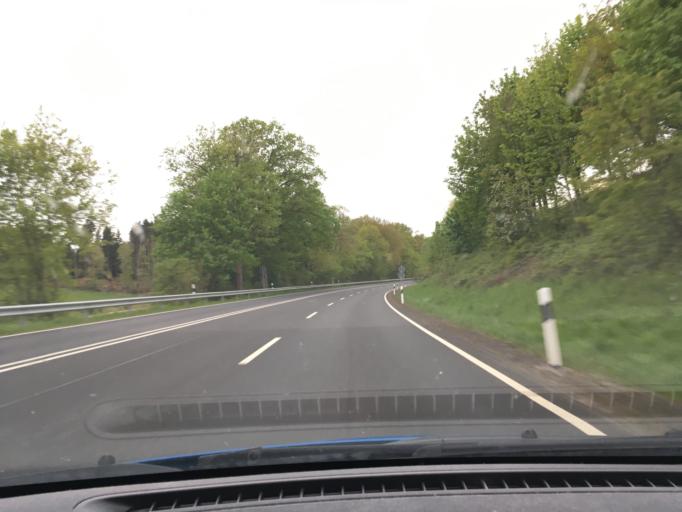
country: DE
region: Lower Saxony
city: Hardegsen
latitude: 51.6322
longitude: 9.7850
